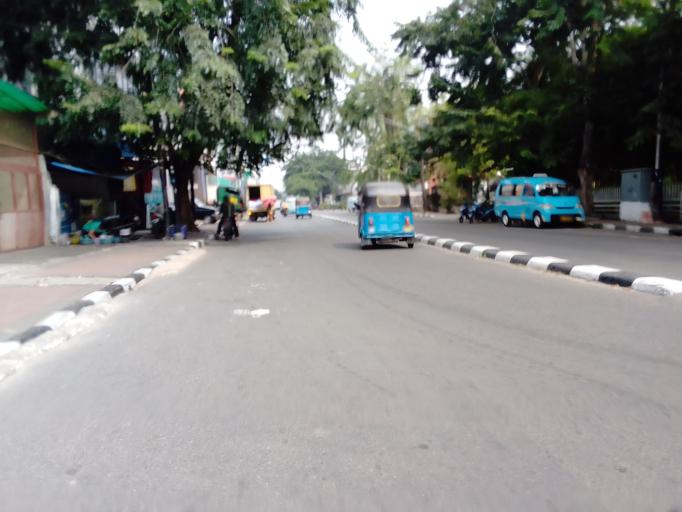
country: ID
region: Jakarta Raya
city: Jakarta
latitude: -6.1639
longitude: 106.8082
